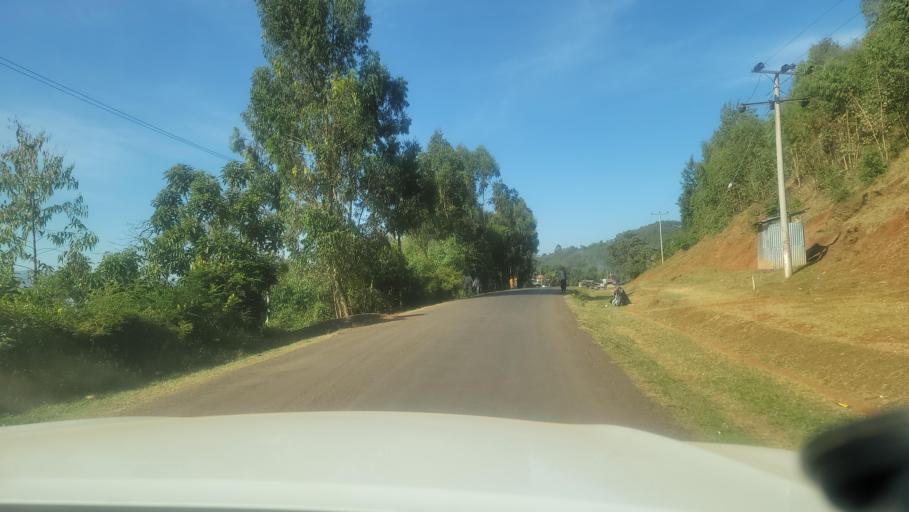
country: ET
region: Oromiya
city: Agaro
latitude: 7.7954
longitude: 36.4824
